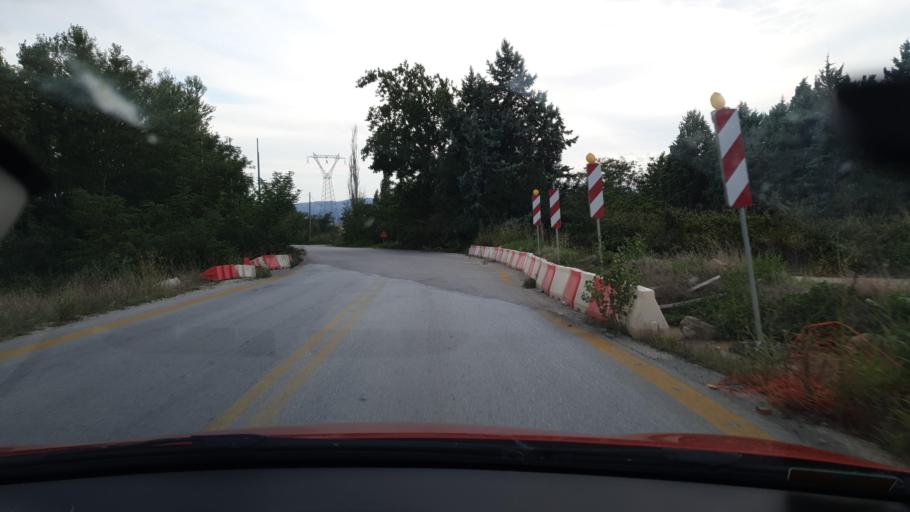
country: GR
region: Central Macedonia
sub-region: Nomos Thessalonikis
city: Assiros
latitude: 40.7861
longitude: 23.0041
